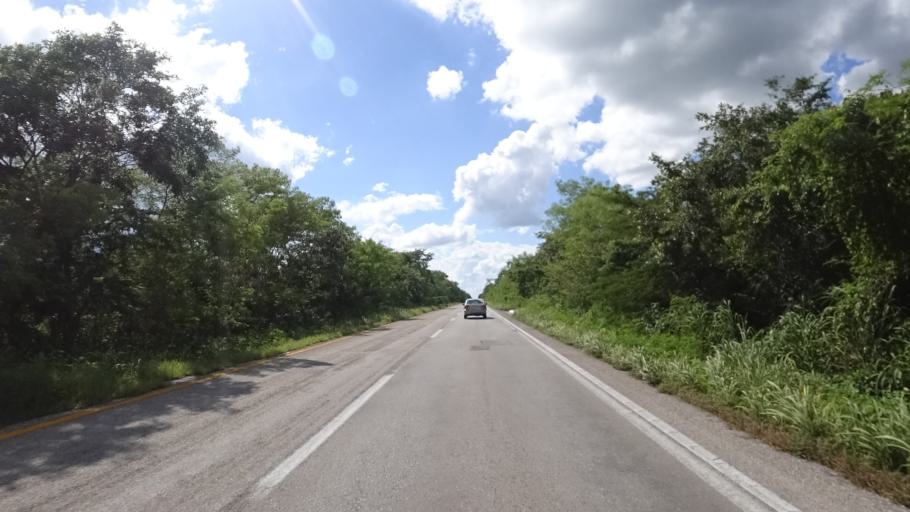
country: MX
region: Yucatan
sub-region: Kantunil
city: Kantunil
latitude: 20.7983
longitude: -88.9911
